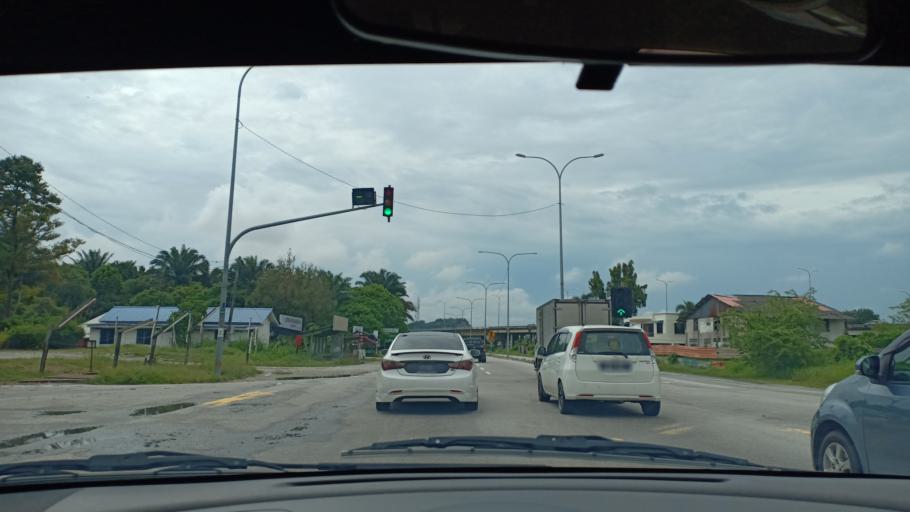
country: MY
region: Penang
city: Bukit Mertajam
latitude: 5.4064
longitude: 100.4899
